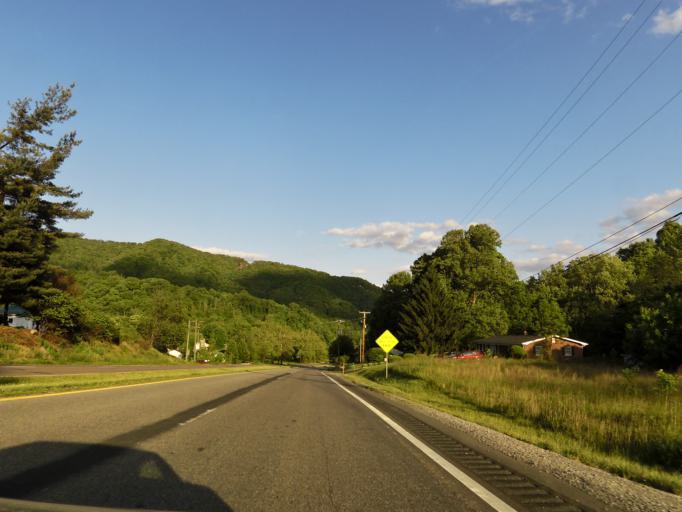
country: US
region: Virginia
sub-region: Russell County
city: Lebanon
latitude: 36.8103
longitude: -82.1026
